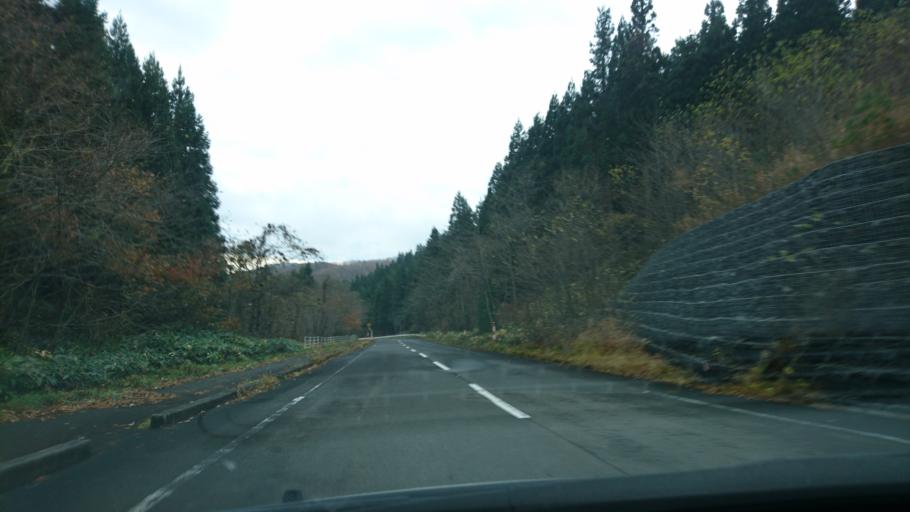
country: JP
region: Iwate
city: Ichinoseki
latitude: 38.9172
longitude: 140.9074
